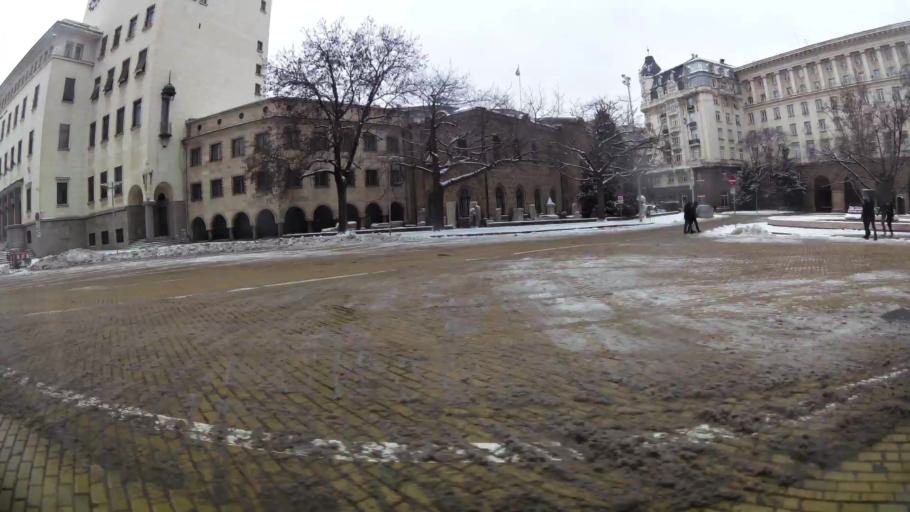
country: BG
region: Sofia-Capital
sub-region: Stolichna Obshtina
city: Sofia
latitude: 42.6969
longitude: 23.3249
